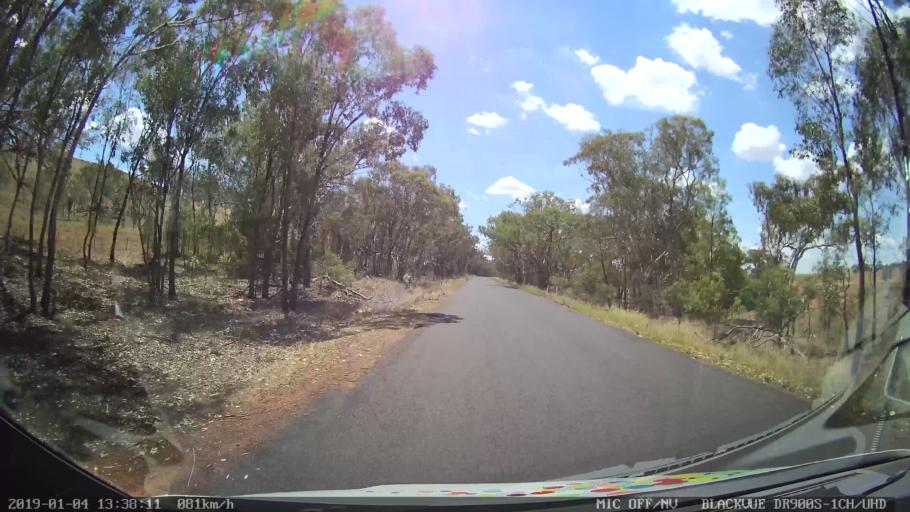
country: AU
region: New South Wales
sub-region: Dubbo Municipality
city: Dubbo
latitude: -32.5410
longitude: 148.5467
